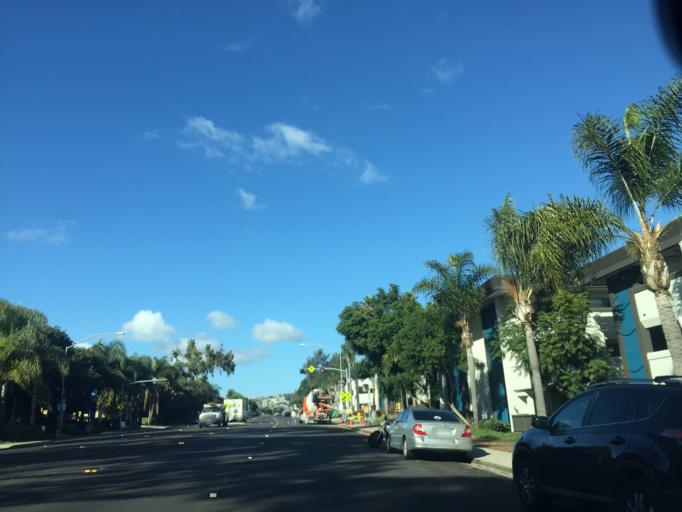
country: US
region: California
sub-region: San Diego County
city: La Jolla
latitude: 32.7899
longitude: -117.2378
